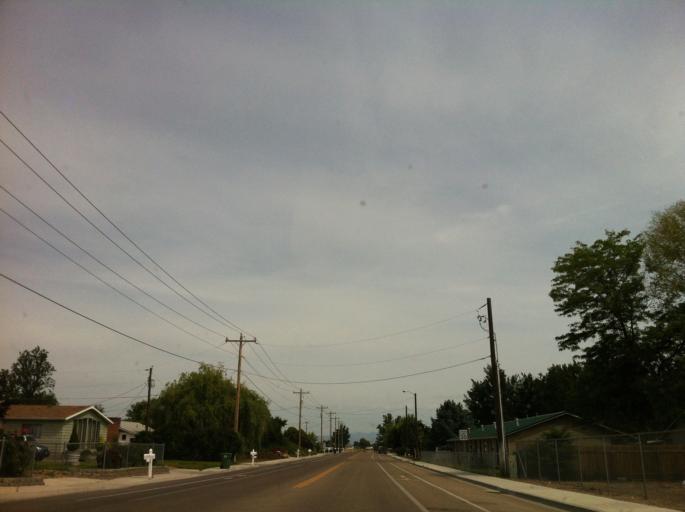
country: US
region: Idaho
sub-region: Payette County
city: Fruitland
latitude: 44.0252
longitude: -116.9332
